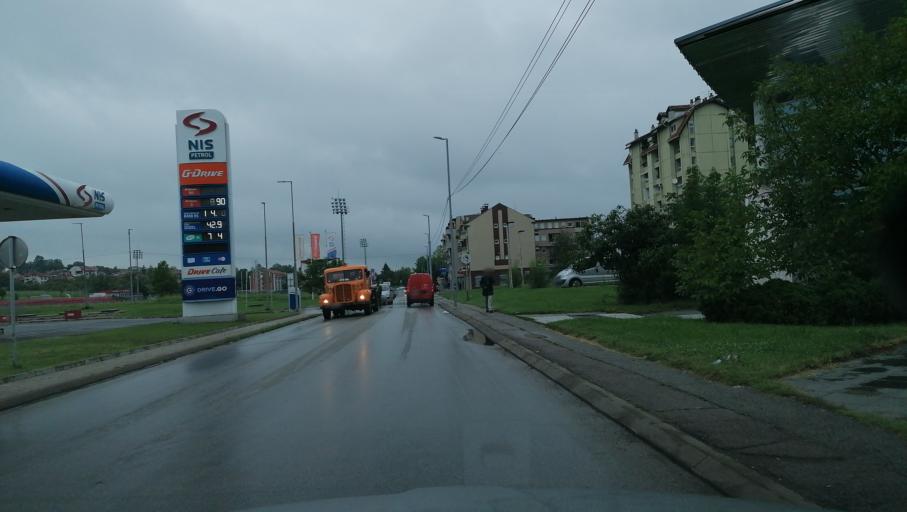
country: RS
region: Central Serbia
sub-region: Rasinski Okrug
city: Krusevac
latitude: 43.5717
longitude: 21.3297
